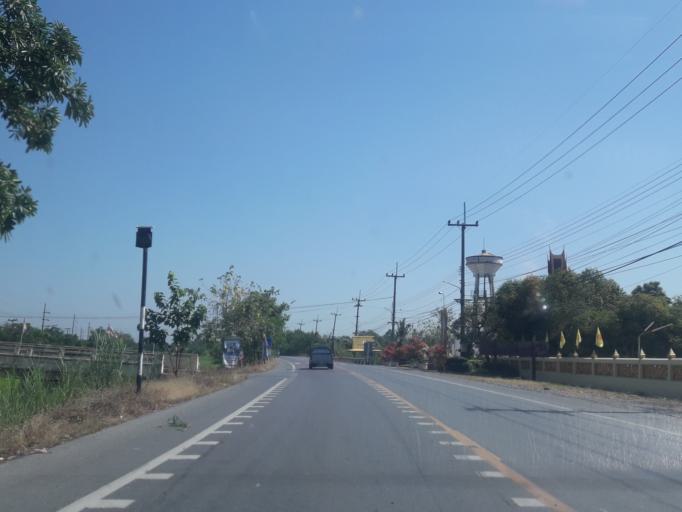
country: TH
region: Sara Buri
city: Nong Khae
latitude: 14.3171
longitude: 100.8627
